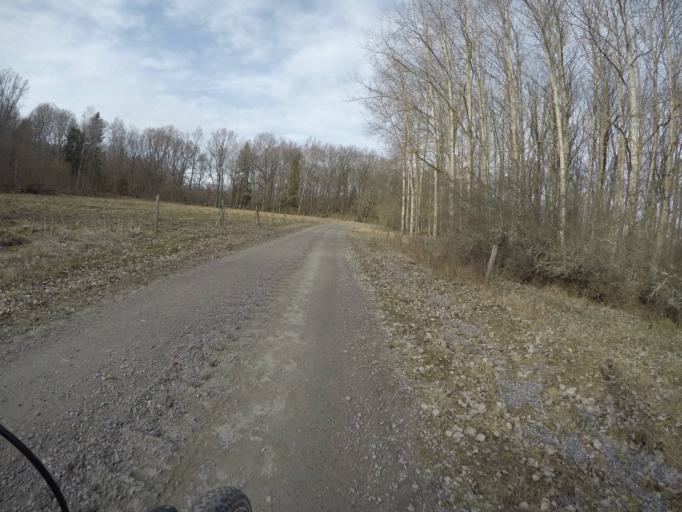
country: SE
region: Soedermanland
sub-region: Eskilstuna Kommun
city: Hallbybrunn
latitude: 59.4474
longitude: 16.3939
